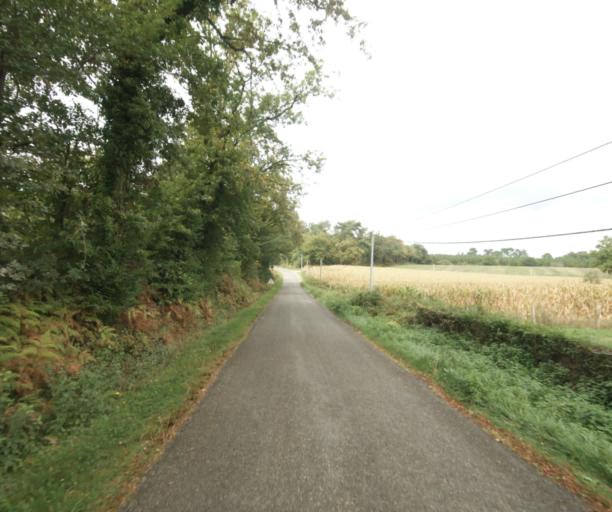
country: FR
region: Midi-Pyrenees
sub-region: Departement du Gers
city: Cazaubon
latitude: 43.8817
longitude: -0.1013
